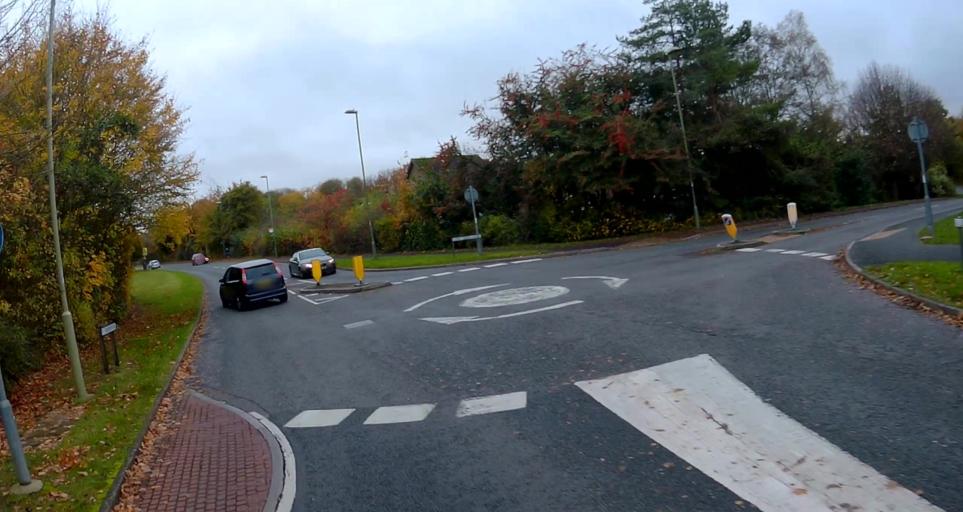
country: GB
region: England
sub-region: Hampshire
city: Basingstoke
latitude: 51.2337
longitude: -1.1321
